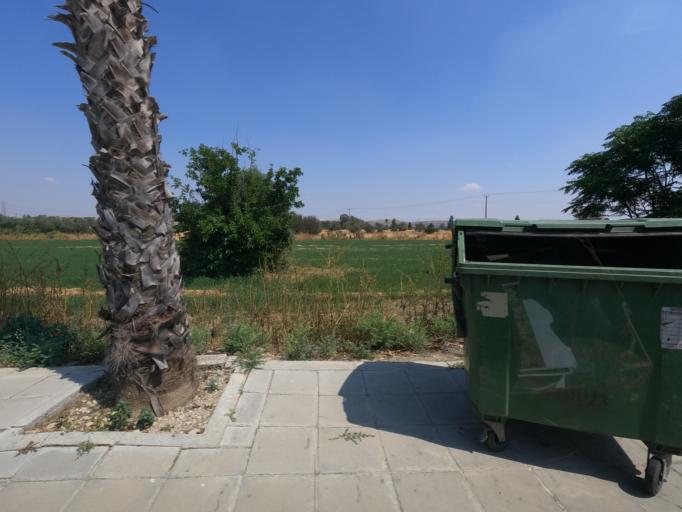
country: CY
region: Lefkosia
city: Dali
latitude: 35.0398
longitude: 33.4411
